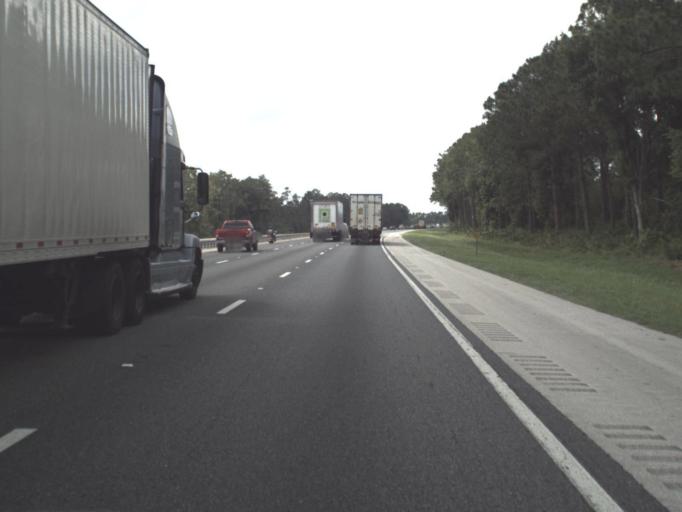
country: US
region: Florida
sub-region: Saint Johns County
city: Saint Augustine South
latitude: 29.8491
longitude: -81.3906
